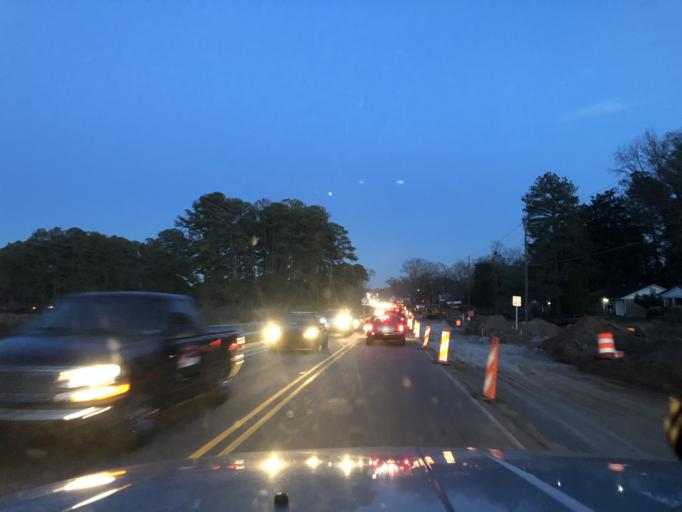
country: US
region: Georgia
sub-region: Clayton County
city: Jonesboro
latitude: 33.5183
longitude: -84.3906
